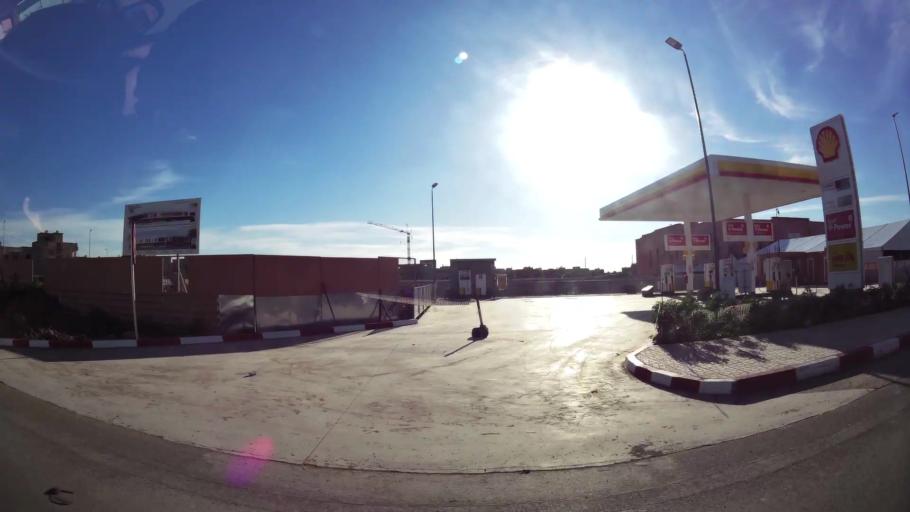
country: MA
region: Marrakech-Tensift-Al Haouz
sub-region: Marrakech
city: Marrakesh
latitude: 31.6789
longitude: -8.0599
